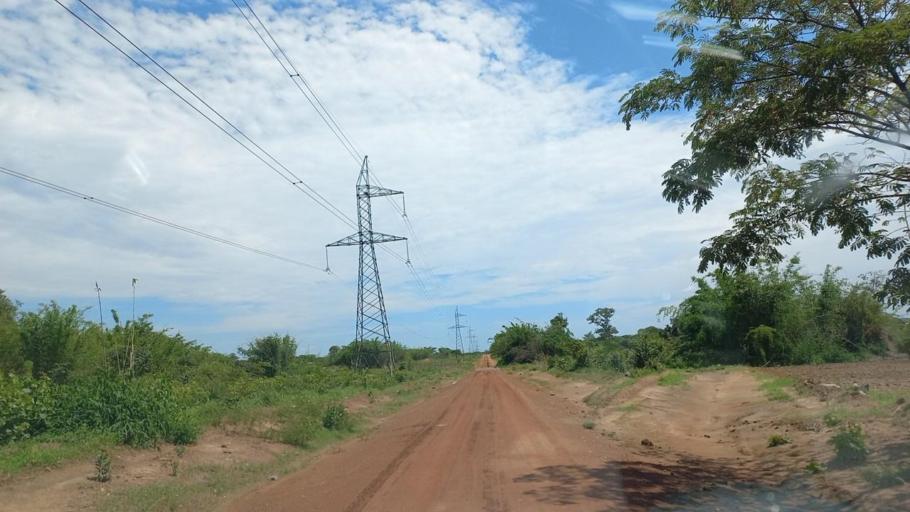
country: ZM
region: Copperbelt
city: Kitwe
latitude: -12.8242
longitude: 28.3504
